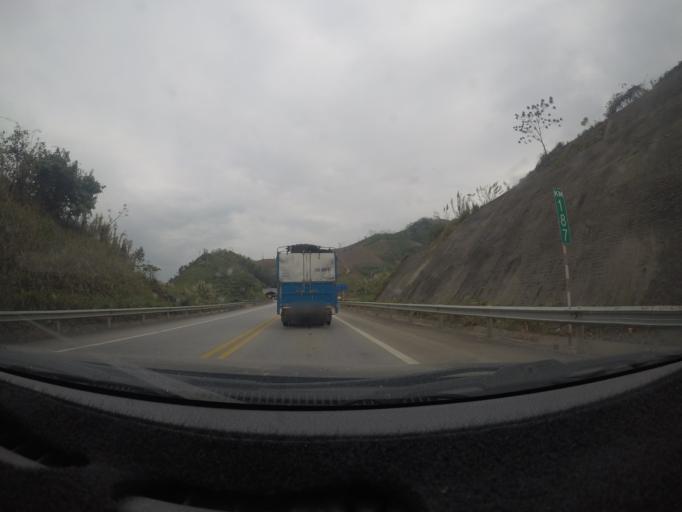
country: VN
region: Lao Cai
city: Thi Tran Pho Rang
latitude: 22.0973
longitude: 104.4257
